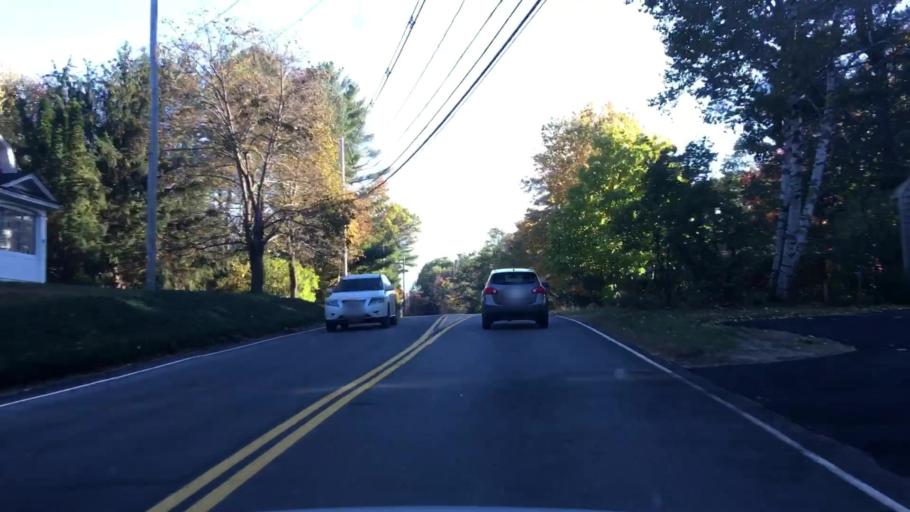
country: US
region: Maine
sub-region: Cumberland County
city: South Portland Gardens
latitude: 43.6134
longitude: -70.3411
